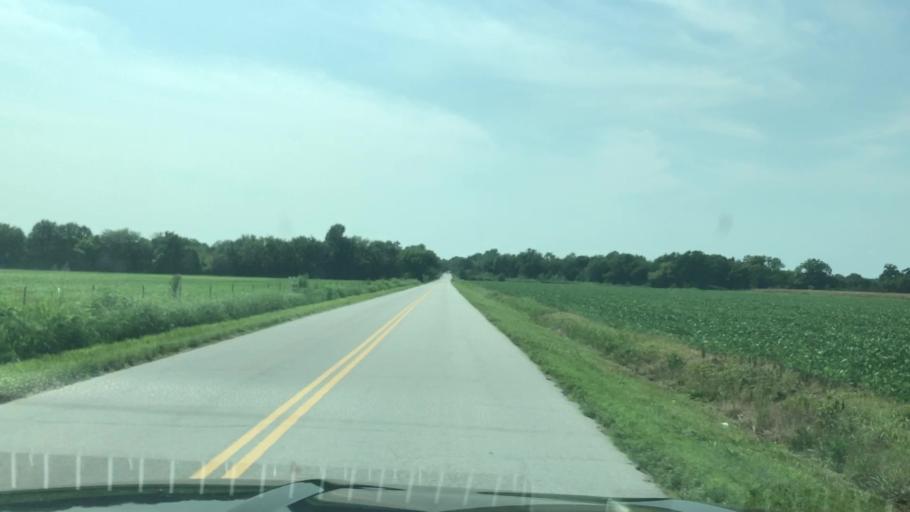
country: US
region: Oklahoma
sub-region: Ottawa County
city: Commerce
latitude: 36.9292
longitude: -94.8524
